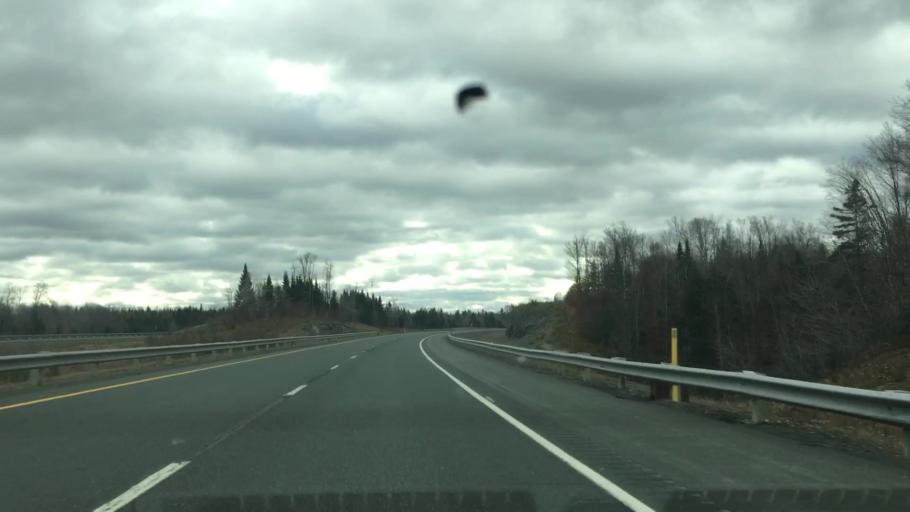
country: US
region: Maine
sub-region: Aroostook County
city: Easton
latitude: 46.6225
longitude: -67.7388
